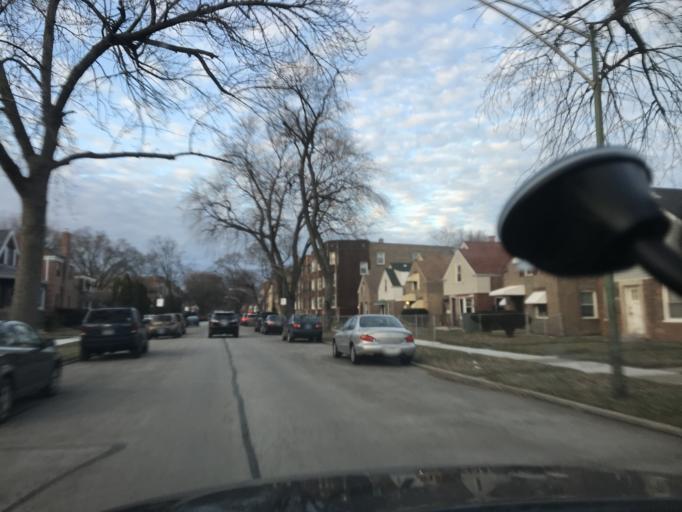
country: US
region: Illinois
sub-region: Cook County
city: Burnham
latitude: 41.7377
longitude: -87.5782
